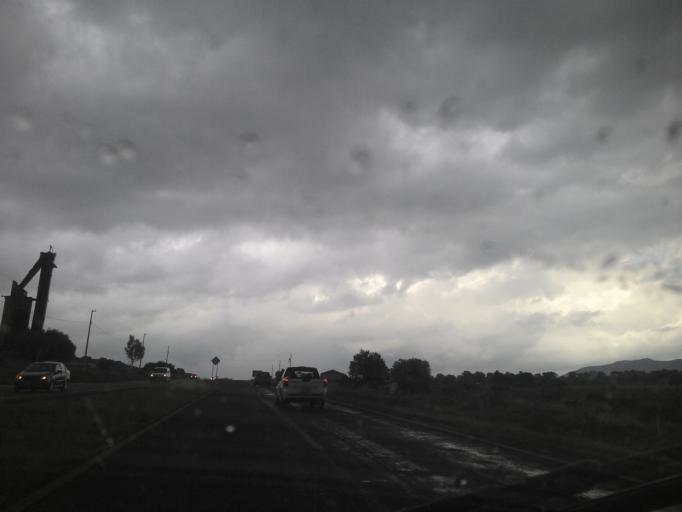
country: MX
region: Hidalgo
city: Zempoala
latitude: 19.9078
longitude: -98.5960
